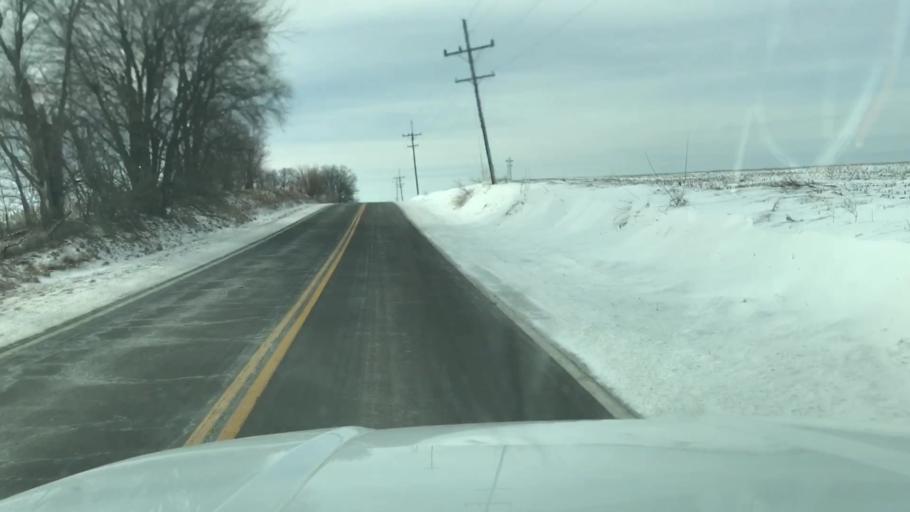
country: US
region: Missouri
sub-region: Holt County
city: Oregon
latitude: 40.0531
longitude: -95.1357
